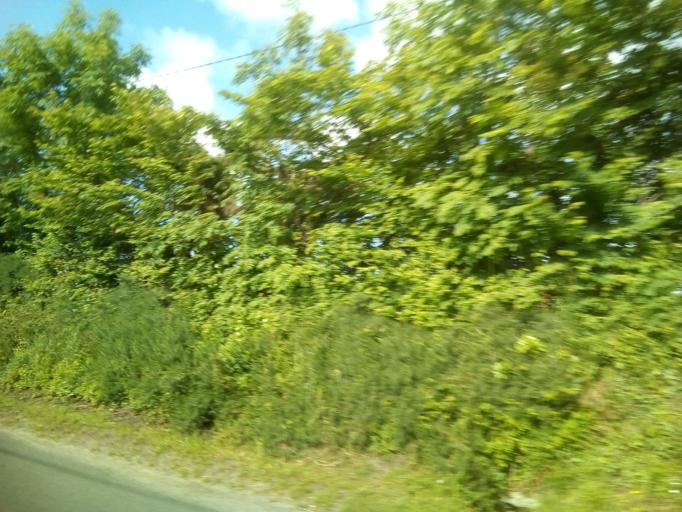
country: IE
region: Leinster
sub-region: Loch Garman
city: Loch Garman
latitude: 52.2479
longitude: -6.5501
